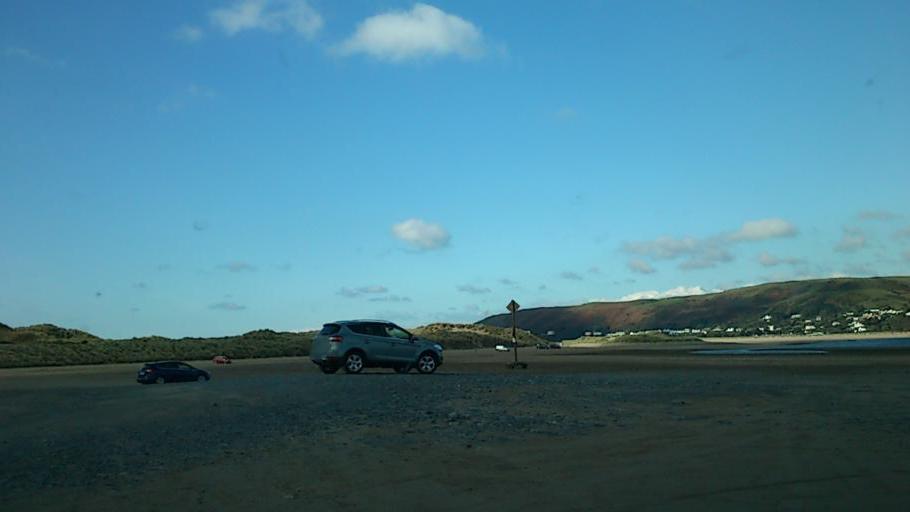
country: GB
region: Wales
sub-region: Gwynedd
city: Tywyn
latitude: 52.5274
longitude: -4.0494
